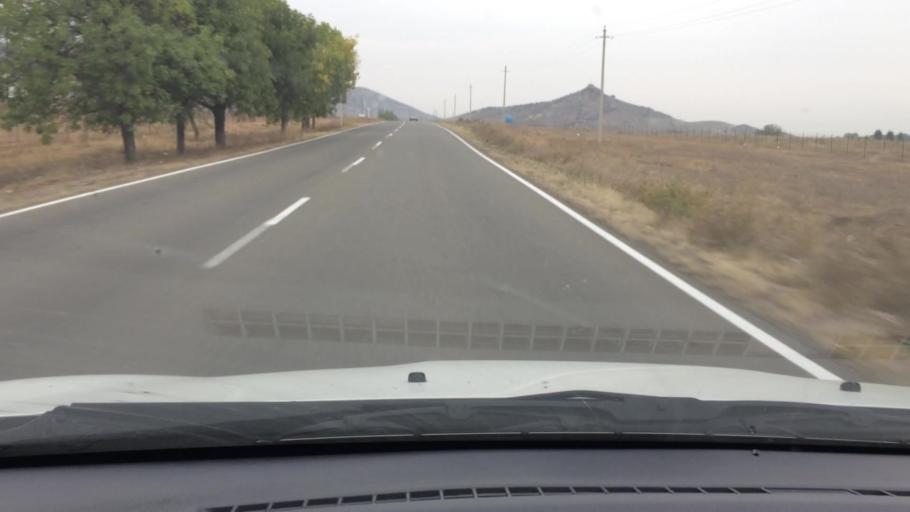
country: GE
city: Naghvarevi
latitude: 41.3426
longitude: 44.8134
